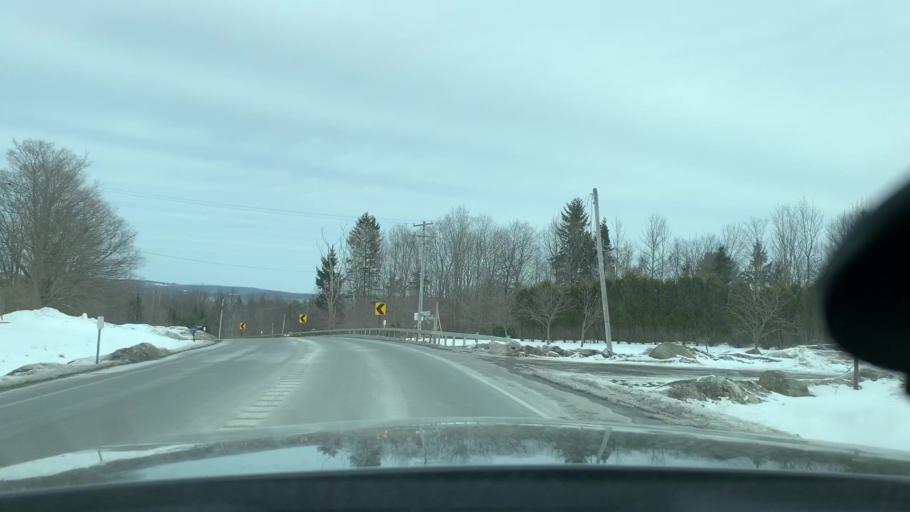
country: US
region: New York
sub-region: Herkimer County
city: Frankfort
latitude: 43.0333
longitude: -75.1043
